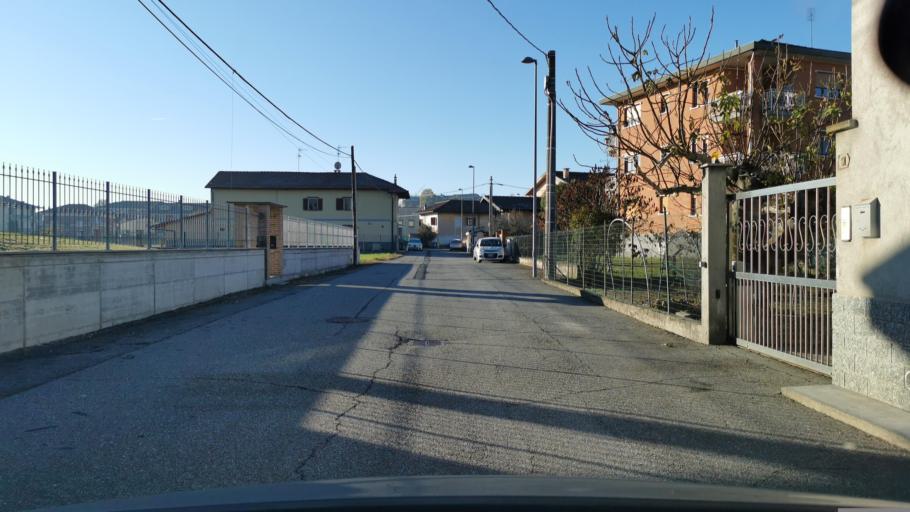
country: IT
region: Piedmont
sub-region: Provincia di Torino
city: Volpiano
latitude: 45.2088
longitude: 7.7749
